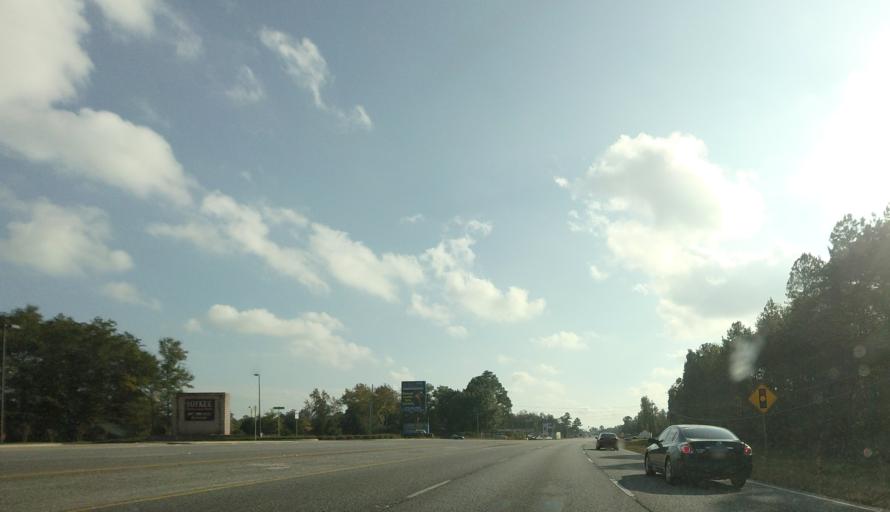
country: US
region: Georgia
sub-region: Bibb County
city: Macon
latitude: 32.7440
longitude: -83.6552
